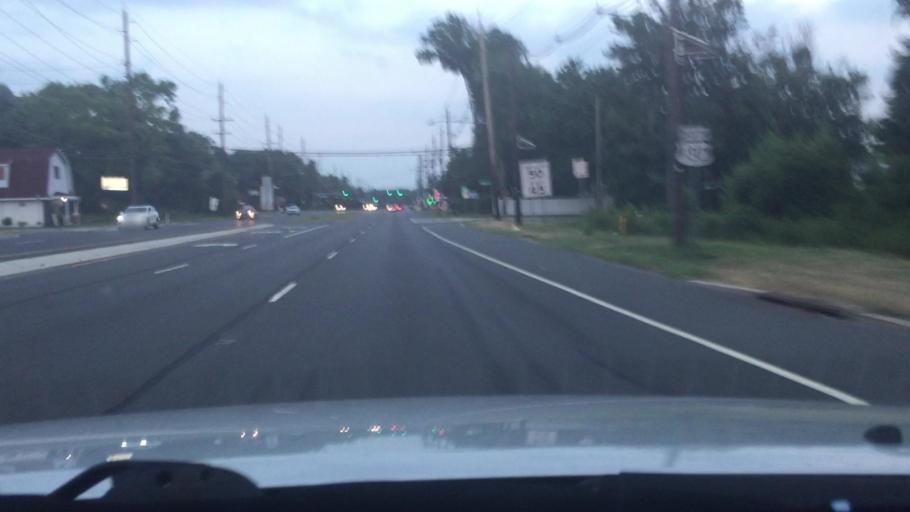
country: US
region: New Jersey
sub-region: Middlesex County
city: Milltown
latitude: 40.4417
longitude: -74.4747
